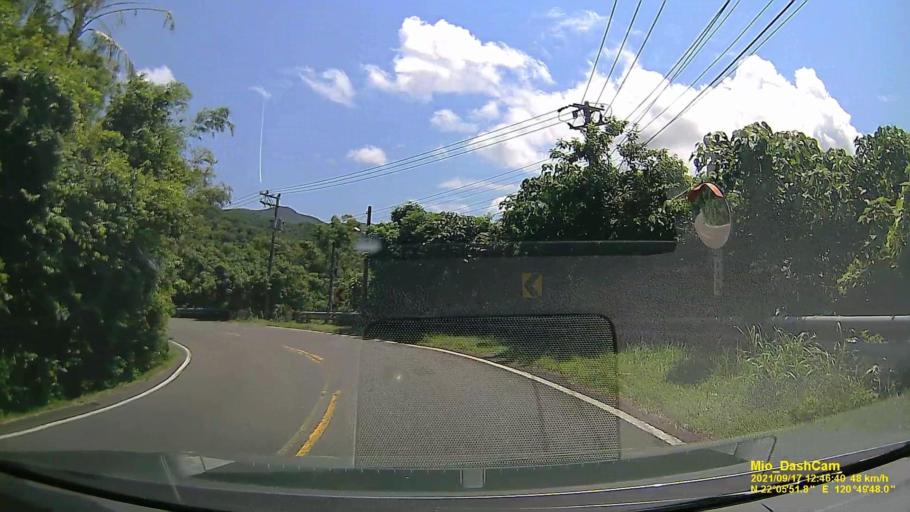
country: TW
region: Taiwan
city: Hengchun
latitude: 22.0976
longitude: 120.8300
